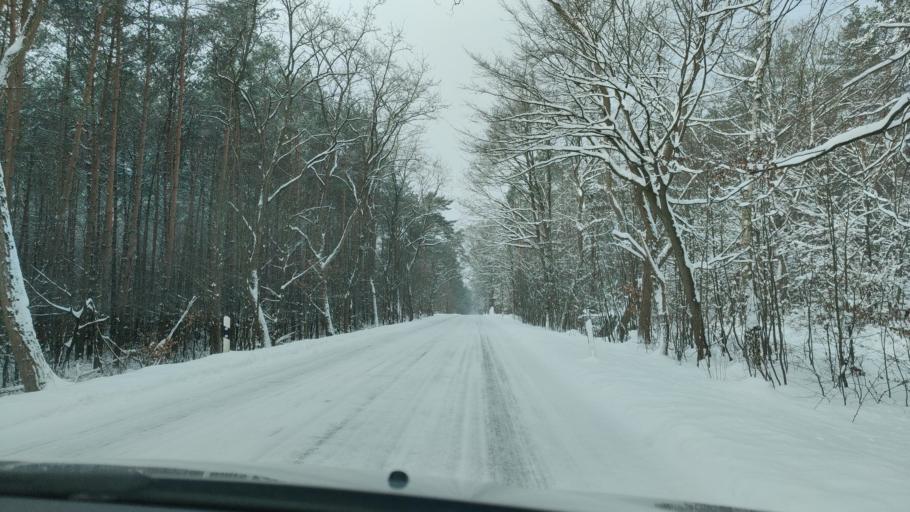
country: DE
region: Saxony
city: Bad Duben
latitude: 51.6505
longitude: 12.6040
